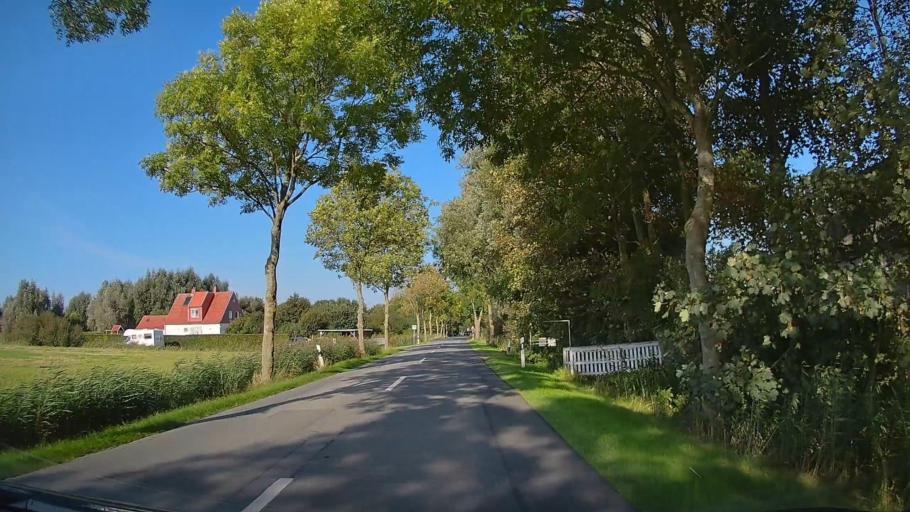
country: DE
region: Lower Saxony
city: Padingbuttel
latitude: 53.7335
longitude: 8.5460
